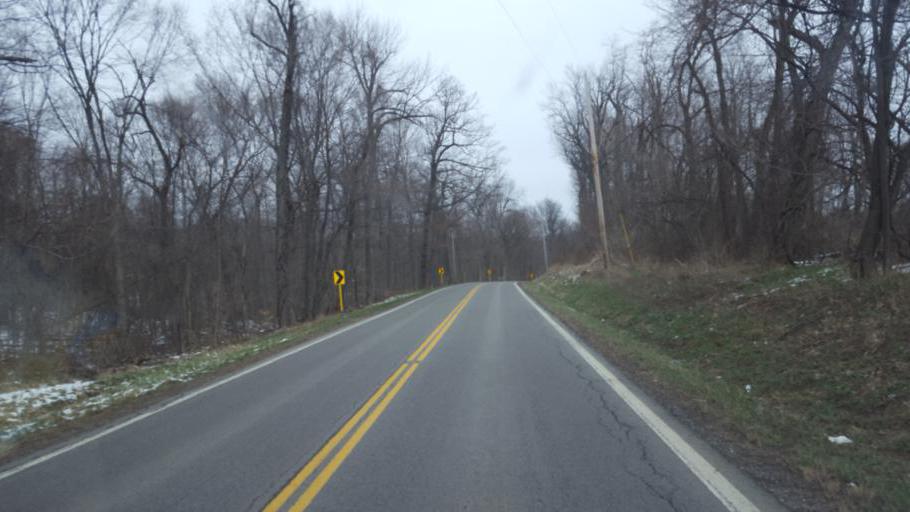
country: US
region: Ohio
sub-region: Richland County
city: Lexington
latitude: 40.6544
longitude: -82.5895
